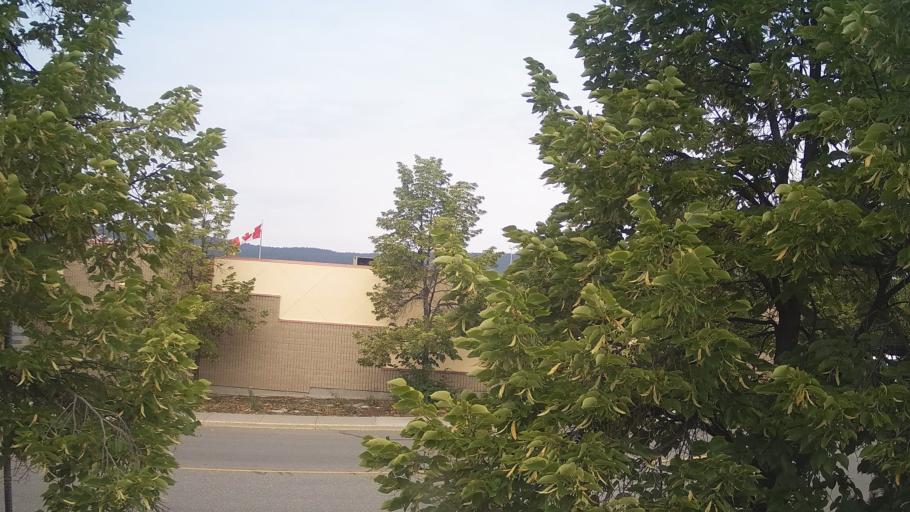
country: CA
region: British Columbia
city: Williams Lake
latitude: 52.1293
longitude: -122.1330
